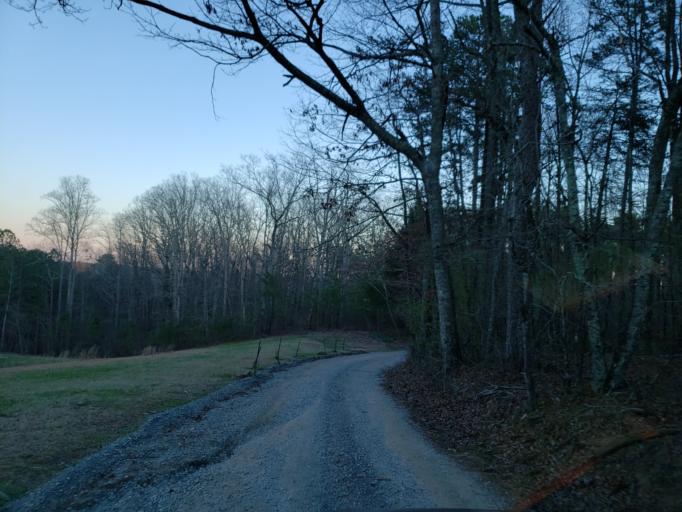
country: US
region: Georgia
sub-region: Pickens County
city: Nelson
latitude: 34.3767
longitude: -84.3628
